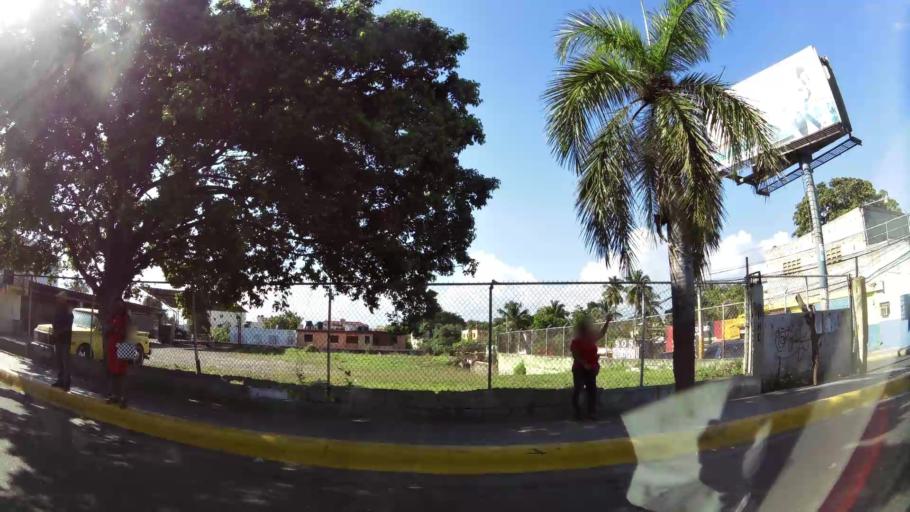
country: DO
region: Nacional
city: Santo Domingo
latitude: 18.4743
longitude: -69.9854
